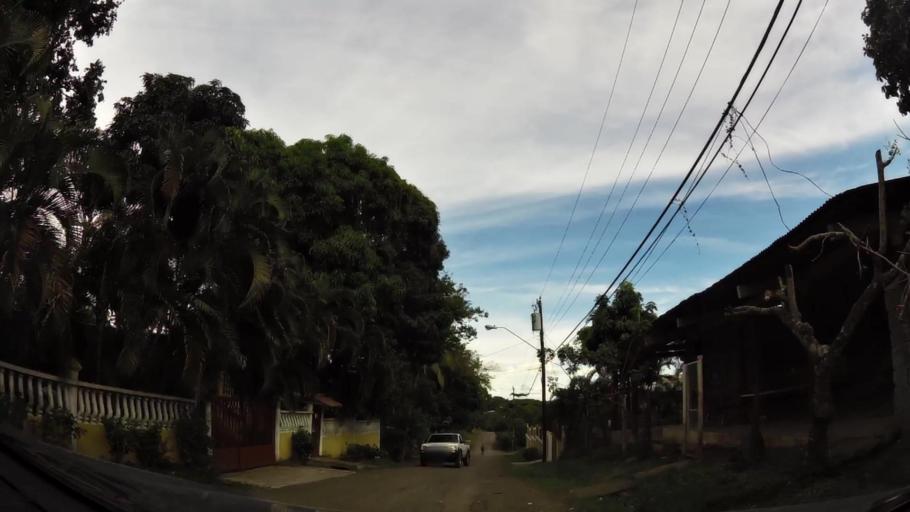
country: PA
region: Panama
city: Guadalupe
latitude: 8.8608
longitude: -79.8144
